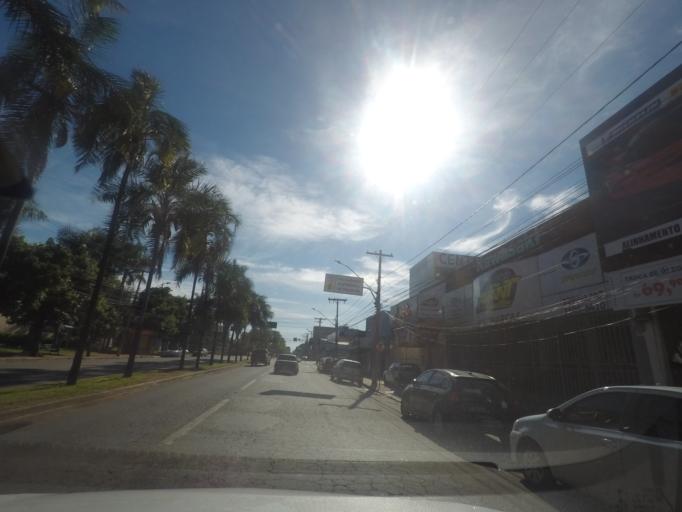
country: BR
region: Goias
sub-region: Goiania
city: Goiania
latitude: -16.6651
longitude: -49.2643
